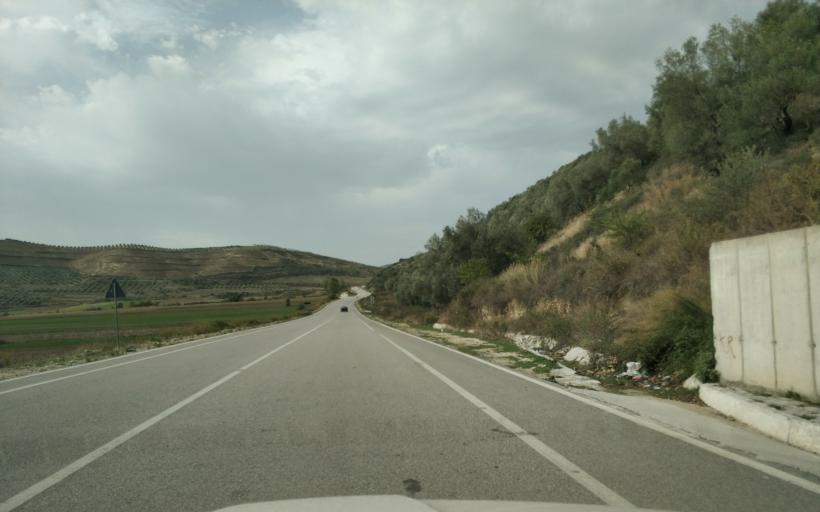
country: AL
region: Gjirokaster
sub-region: Rrethi i Tepelenes
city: Krahes
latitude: 40.3898
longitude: 19.8790
